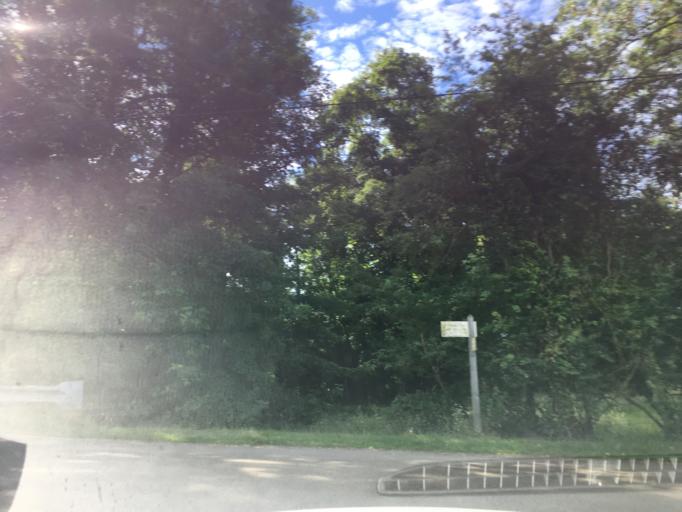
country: FR
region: Bourgogne
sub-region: Departement de l'Yonne
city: Saint-Georges-sur-Baulche
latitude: 47.7740
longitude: 3.5019
